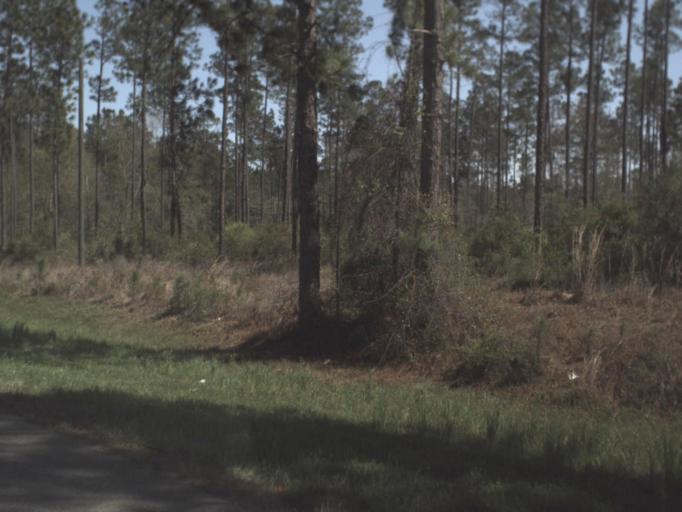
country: US
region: Florida
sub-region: Calhoun County
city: Blountstown
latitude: 30.4281
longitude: -85.1113
